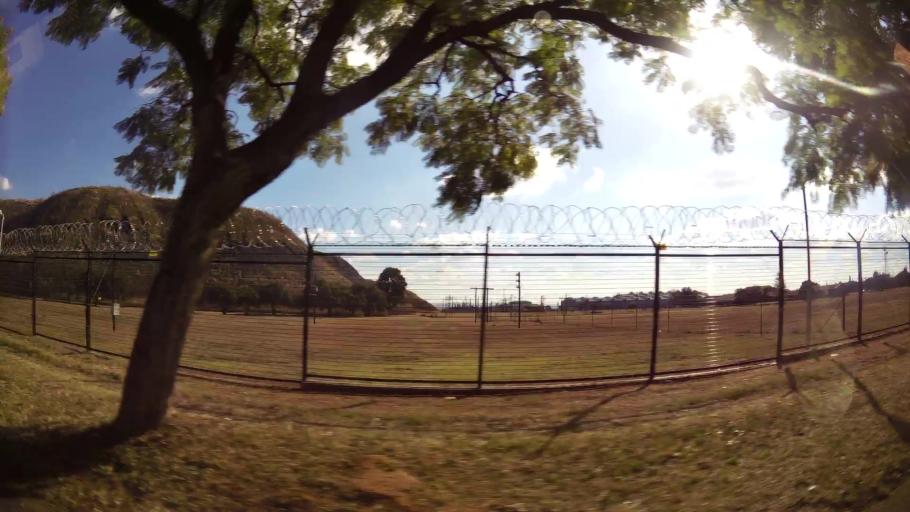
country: ZA
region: Mpumalanga
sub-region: Nkangala District Municipality
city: Witbank
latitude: -25.8930
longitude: 29.2203
